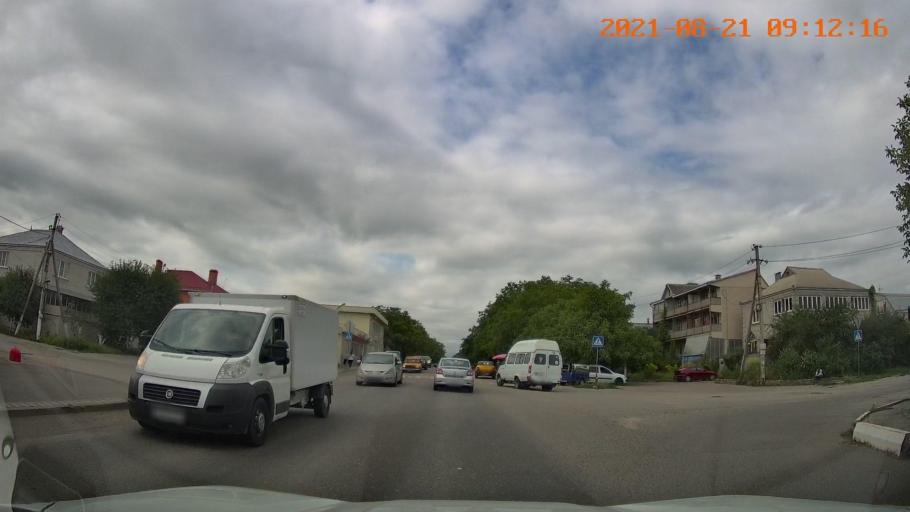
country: RU
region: Stavropol'skiy
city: Svobody
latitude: 44.0141
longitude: 43.0650
